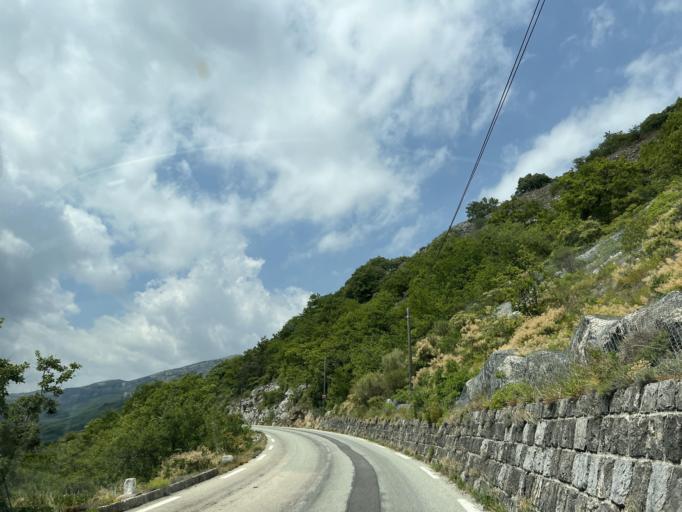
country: FR
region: Provence-Alpes-Cote d'Azur
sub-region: Departement des Alpes-Maritimes
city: Tourrettes-sur-Loup
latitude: 43.7881
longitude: 6.9729
